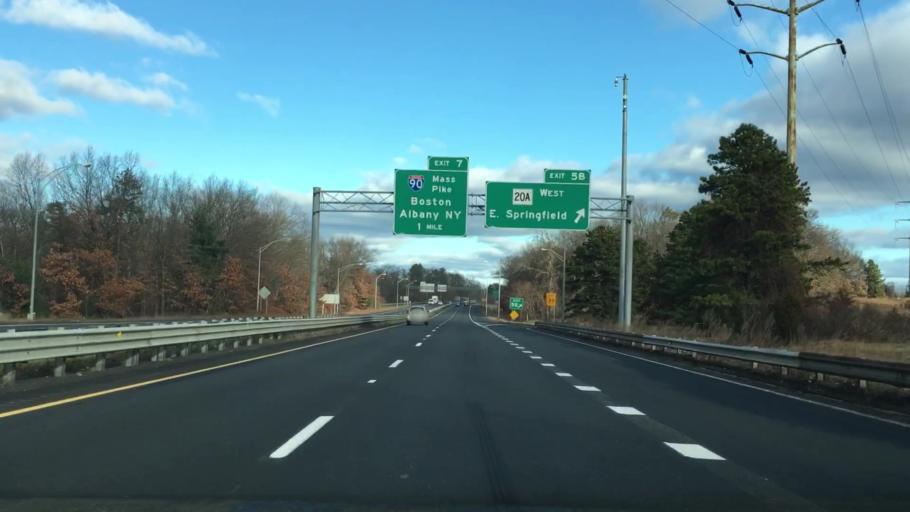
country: US
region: Massachusetts
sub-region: Hampden County
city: Chicopee
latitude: 42.1462
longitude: -72.5493
